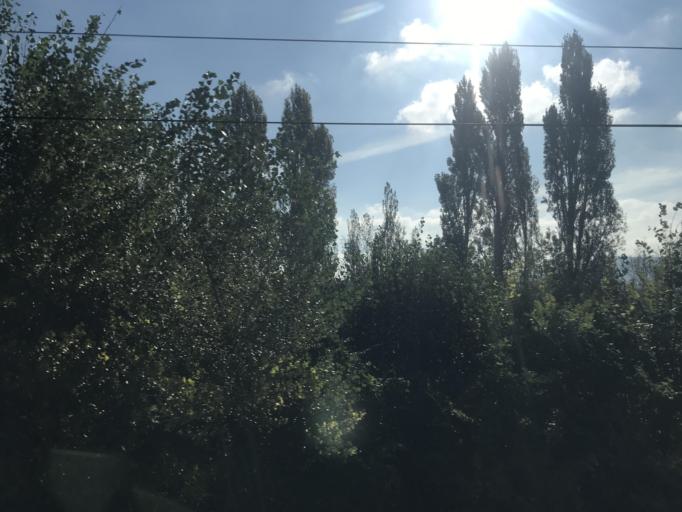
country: ES
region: Basque Country
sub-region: Provincia de Alava
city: Arminon
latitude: 42.7583
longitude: -2.8322
